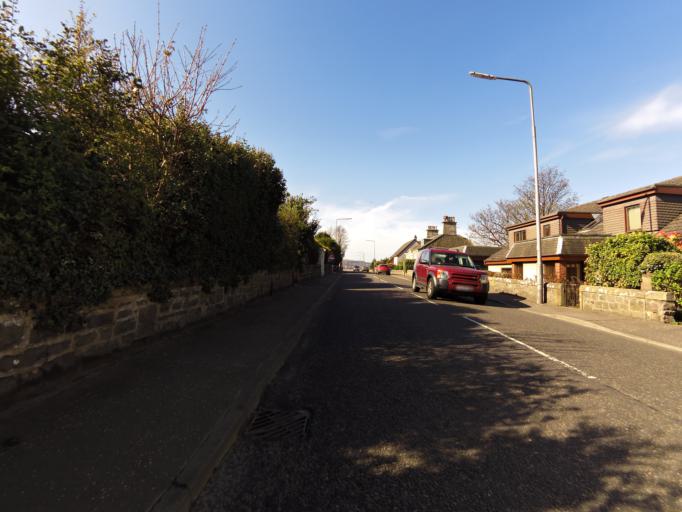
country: GB
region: Scotland
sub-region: Fife
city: Newport-On-Tay
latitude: 56.4443
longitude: -2.9382
